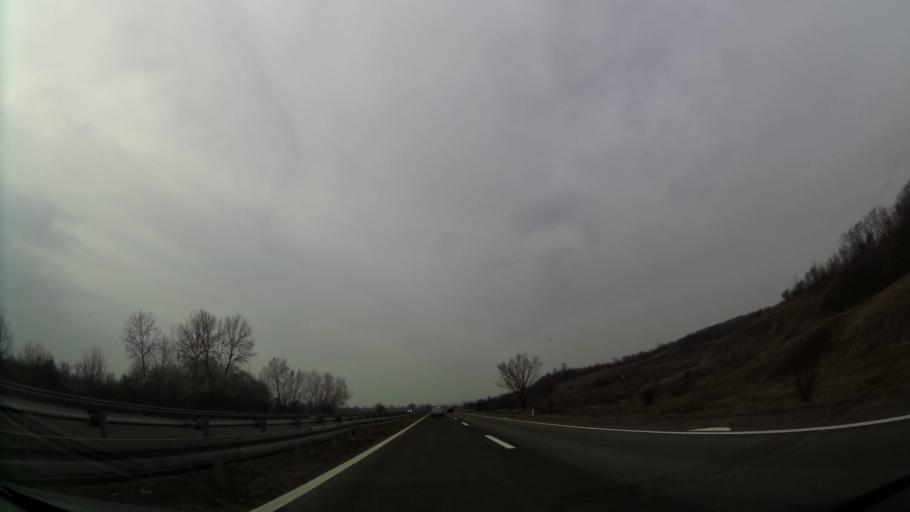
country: RS
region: Central Serbia
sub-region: Nisavski Okrug
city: Aleksinac
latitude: 43.4889
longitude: 21.7664
